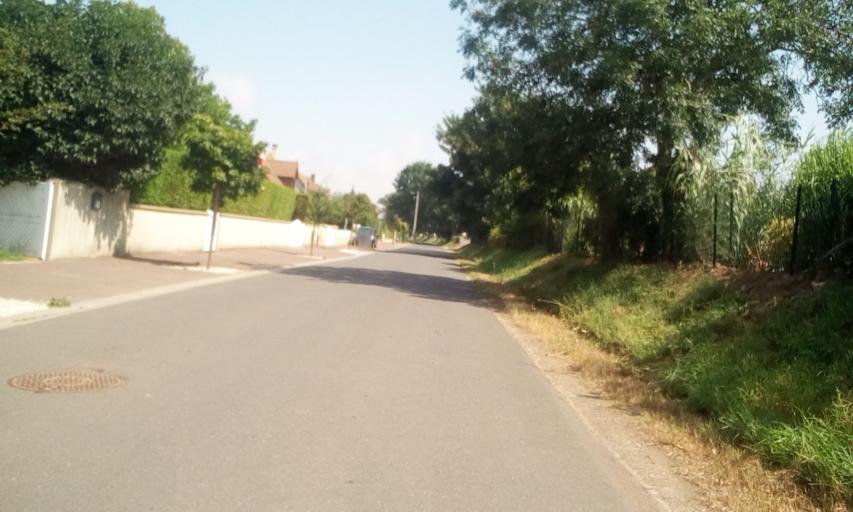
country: FR
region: Lower Normandy
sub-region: Departement du Calvados
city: Bernieres-sur-Mer
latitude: 49.2909
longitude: -0.4313
